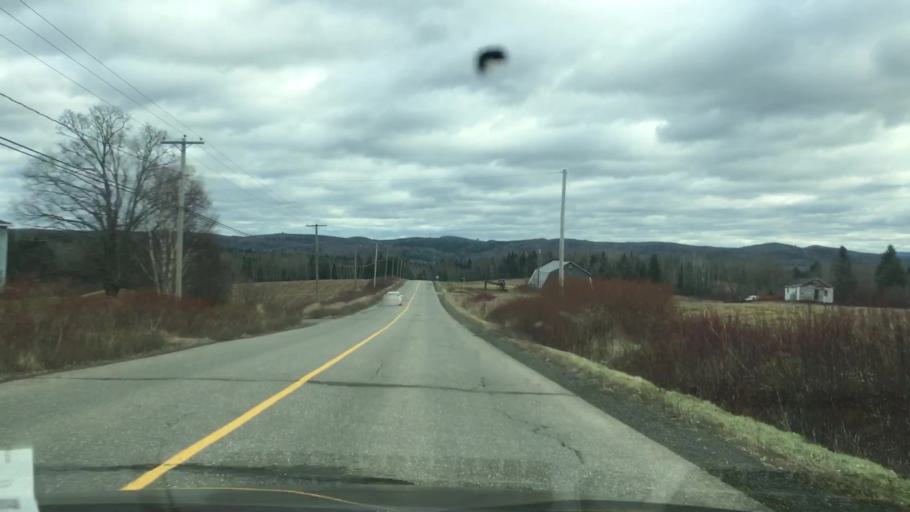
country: US
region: Maine
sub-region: Aroostook County
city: Fort Fairfield
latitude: 46.7493
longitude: -67.7382
